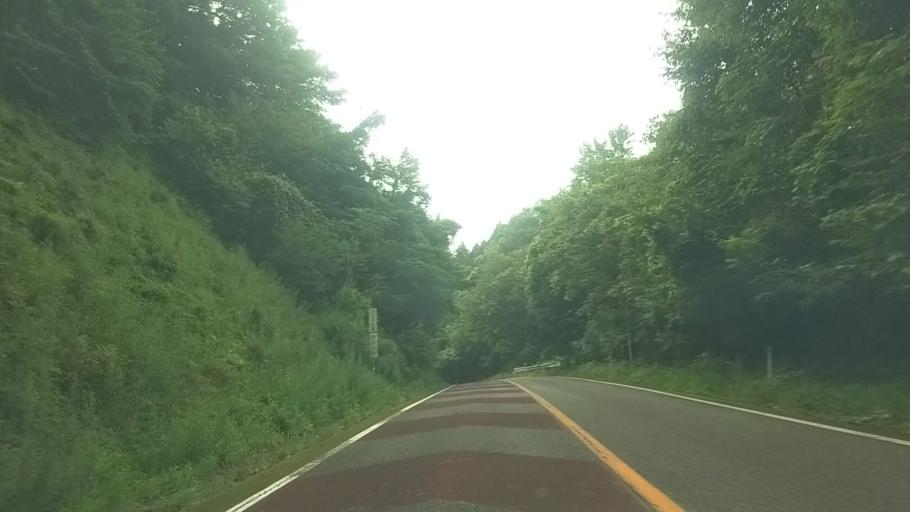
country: JP
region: Chiba
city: Kawaguchi
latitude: 35.2318
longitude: 140.0277
